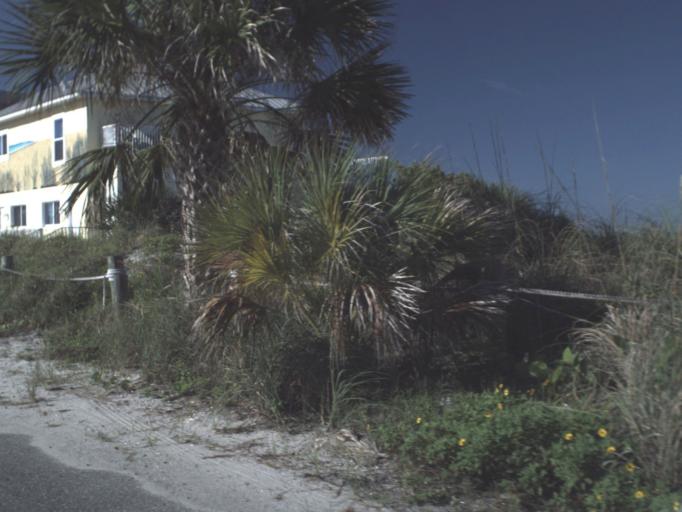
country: US
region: Florida
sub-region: Manatee County
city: Bradenton Beach
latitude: 27.4714
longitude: -82.7007
